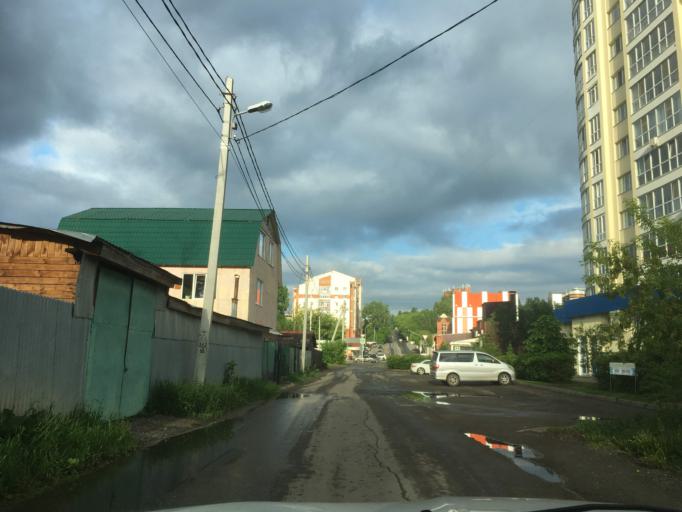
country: RU
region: Tomsk
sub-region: Tomskiy Rayon
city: Tomsk
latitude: 56.4632
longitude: 84.9379
